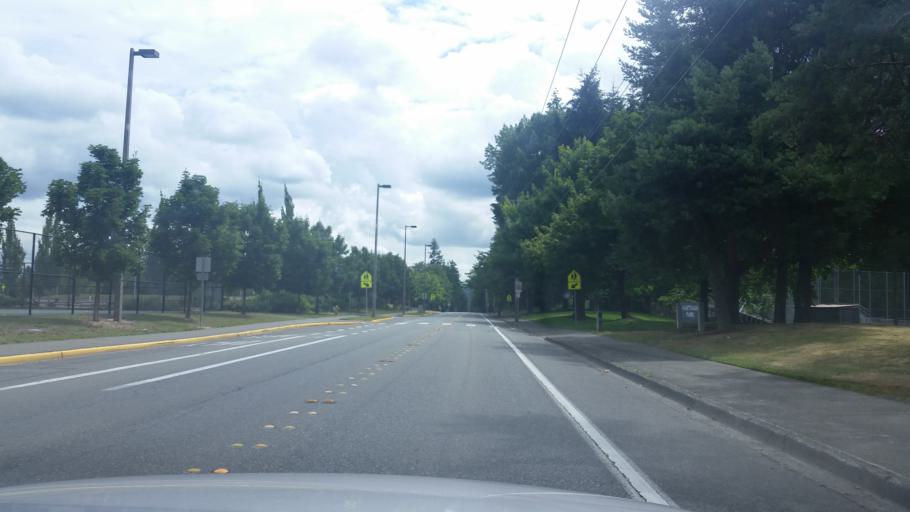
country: US
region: Washington
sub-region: King County
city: Redmond
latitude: 47.6928
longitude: -122.1091
